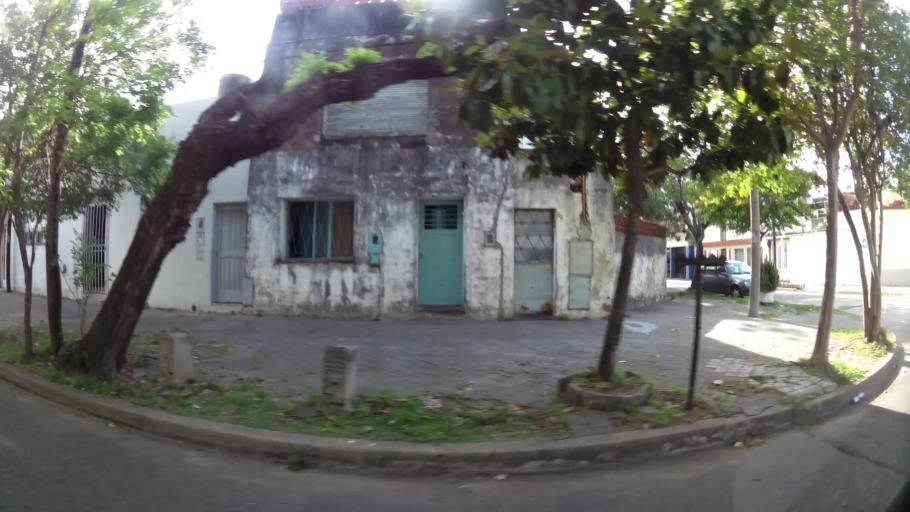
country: AR
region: Santa Fe
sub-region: Departamento de Rosario
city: Rosario
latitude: -32.9257
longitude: -60.6847
